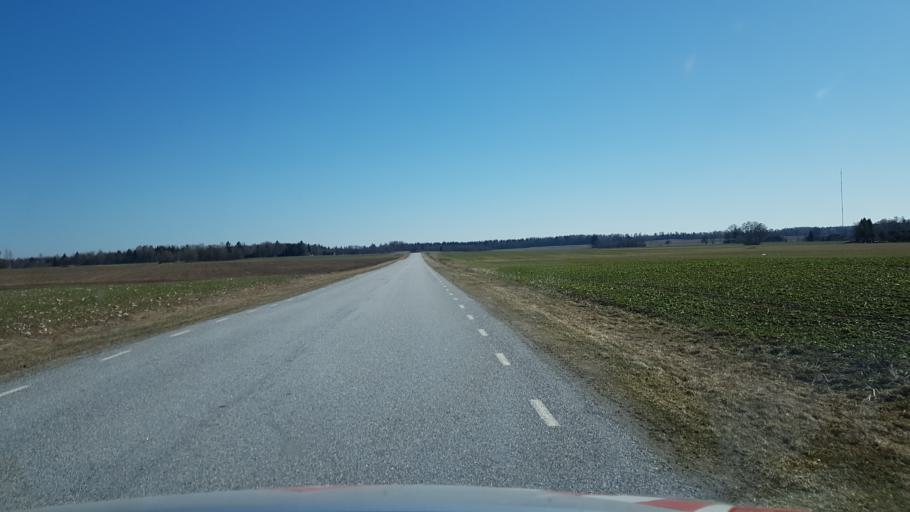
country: EE
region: Jaervamaa
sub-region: Koeru vald
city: Koeru
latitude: 59.0117
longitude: 26.0887
